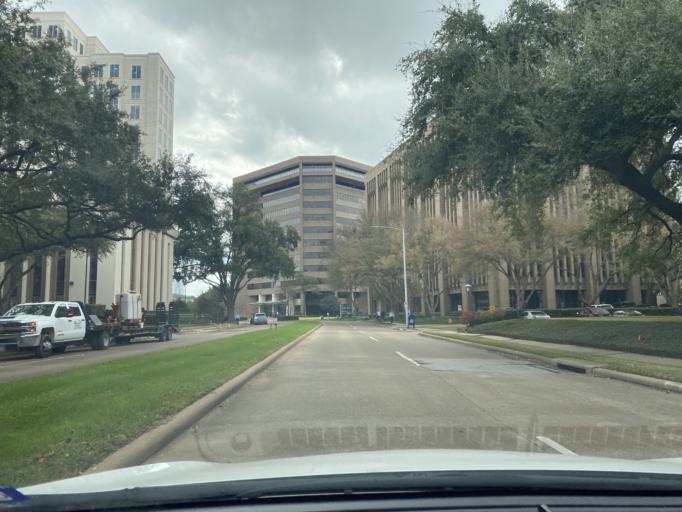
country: US
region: Texas
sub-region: Harris County
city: Hunters Creek Village
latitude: 29.7474
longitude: -95.4732
